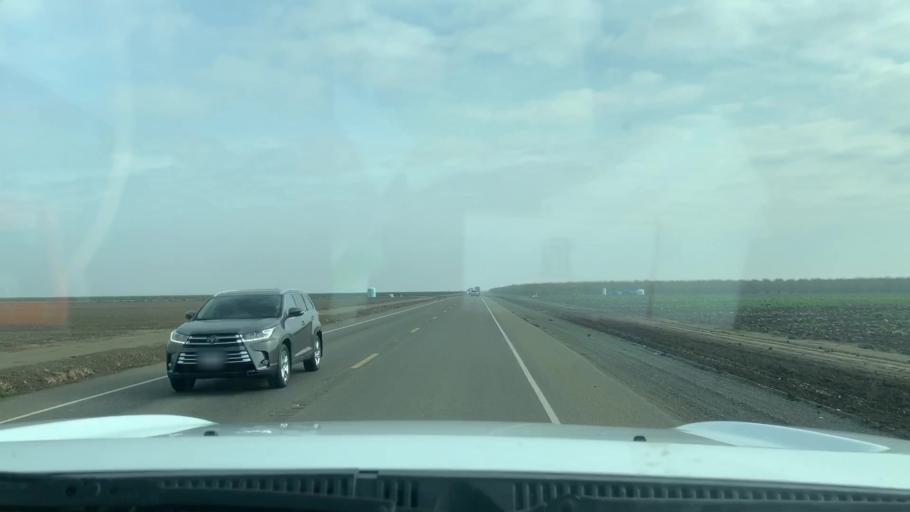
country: US
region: California
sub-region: Fresno County
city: Huron
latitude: 36.2554
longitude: -120.0156
